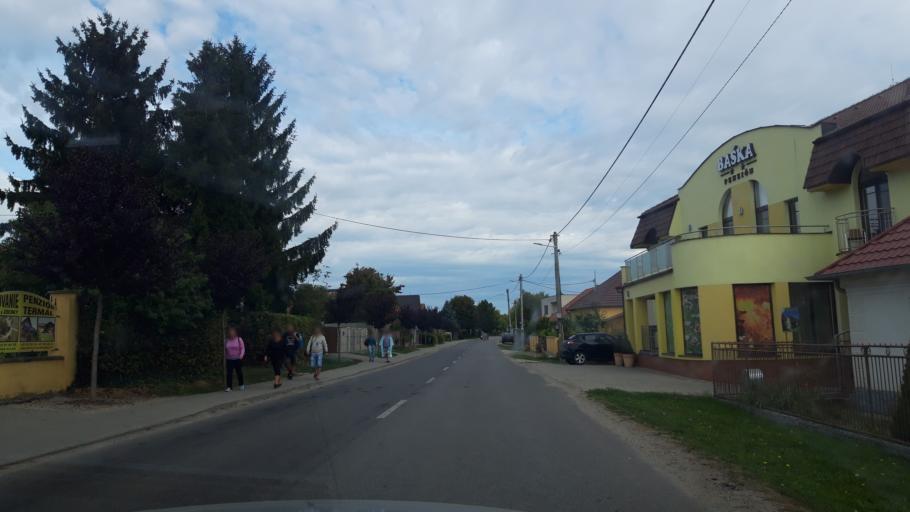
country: SK
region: Nitriansky
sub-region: Okres Nitra
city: Vrable
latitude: 48.1025
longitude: 18.3374
